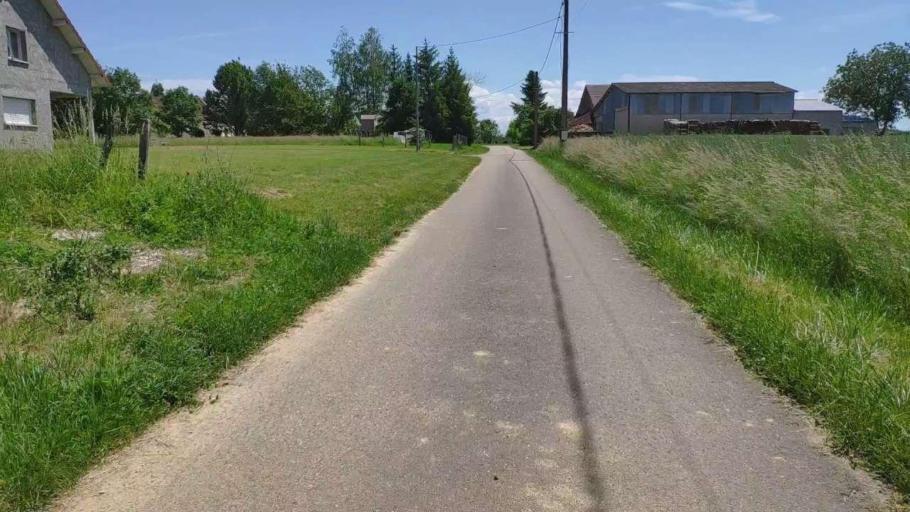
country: FR
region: Franche-Comte
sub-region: Departement du Jura
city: Bletterans
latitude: 46.7990
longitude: 5.3944
